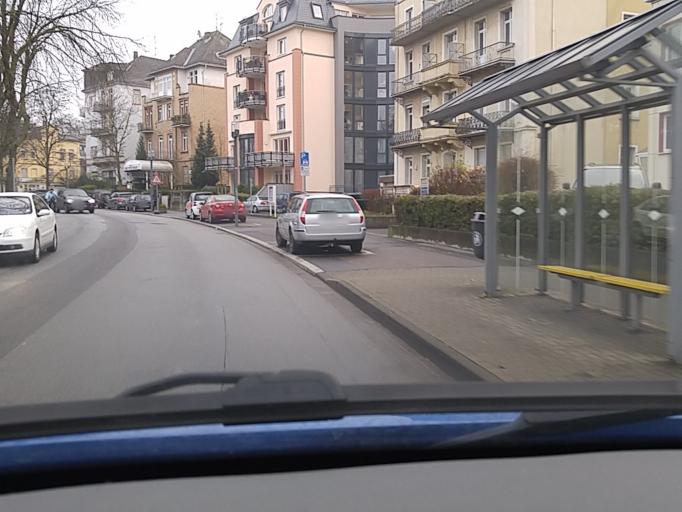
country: DE
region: Hesse
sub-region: Regierungsbezirk Darmstadt
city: Bad Nauheim
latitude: 50.3656
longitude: 8.7444
